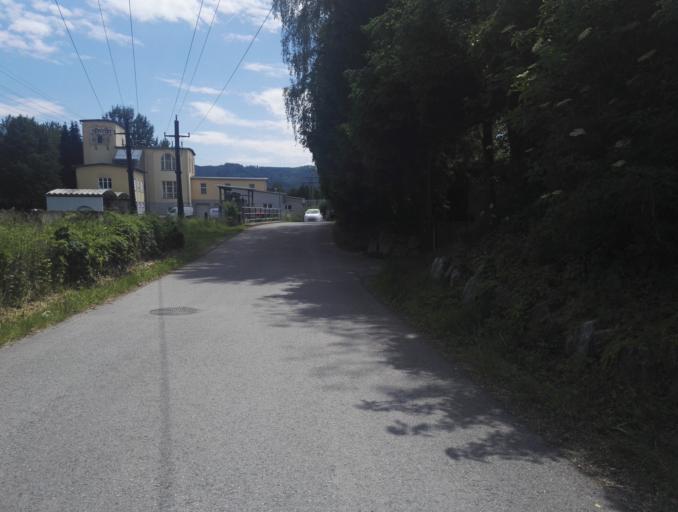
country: AT
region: Styria
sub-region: Politischer Bezirk Graz-Umgebung
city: Gratwein
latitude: 47.1315
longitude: 15.3242
